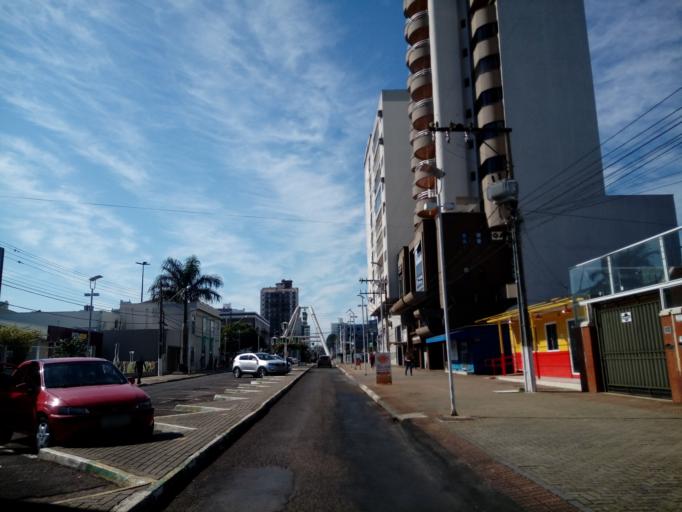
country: BR
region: Santa Catarina
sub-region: Chapeco
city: Chapeco
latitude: -27.0994
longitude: -52.6168
